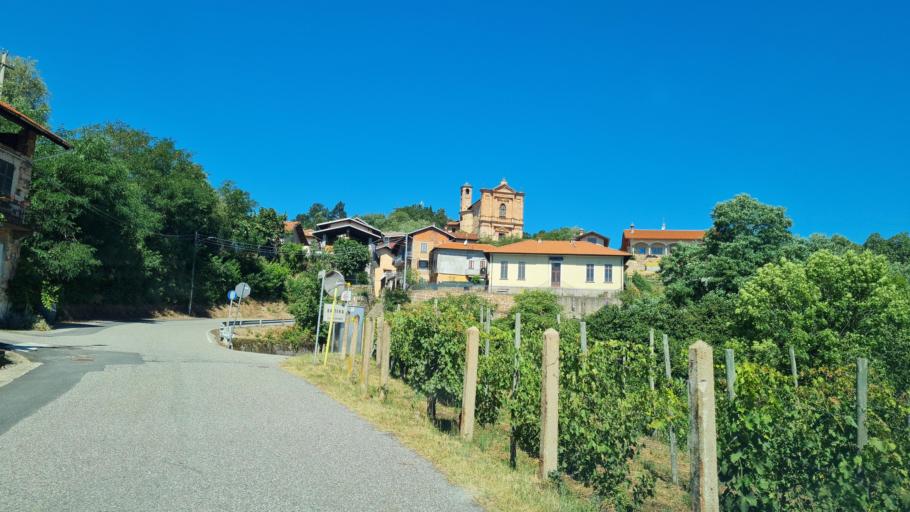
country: IT
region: Piedmont
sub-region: Provincia di Biella
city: Masserano
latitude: 45.5983
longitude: 8.2099
